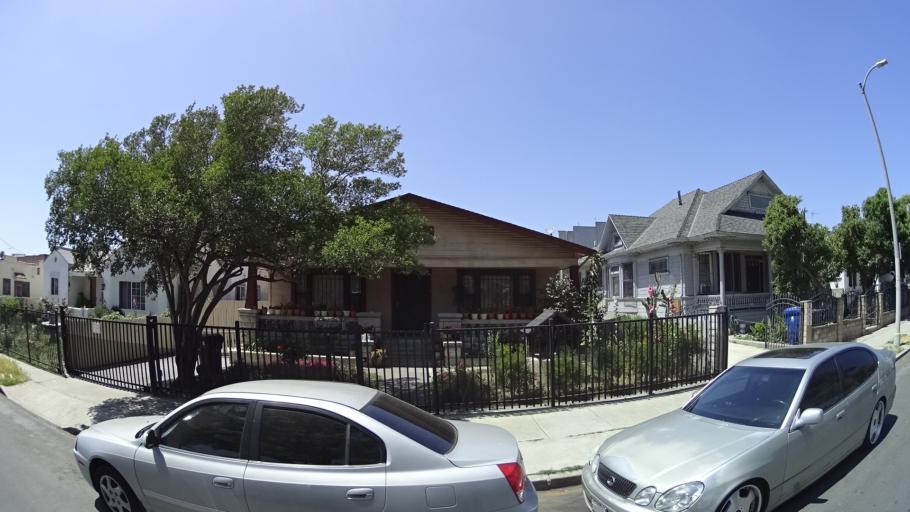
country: US
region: California
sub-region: Los Angeles County
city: Los Angeles
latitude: 34.0749
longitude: -118.2105
